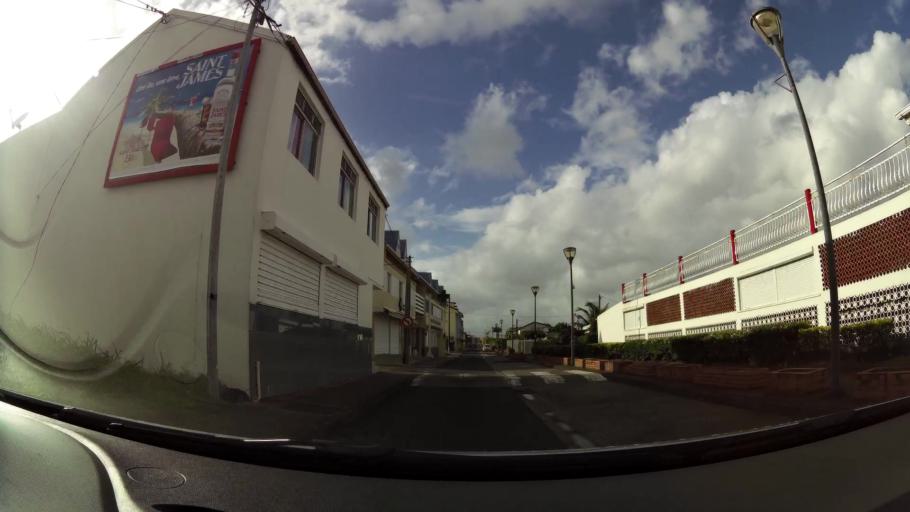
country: MQ
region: Martinique
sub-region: Martinique
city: Ducos
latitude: 14.5275
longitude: -60.9782
